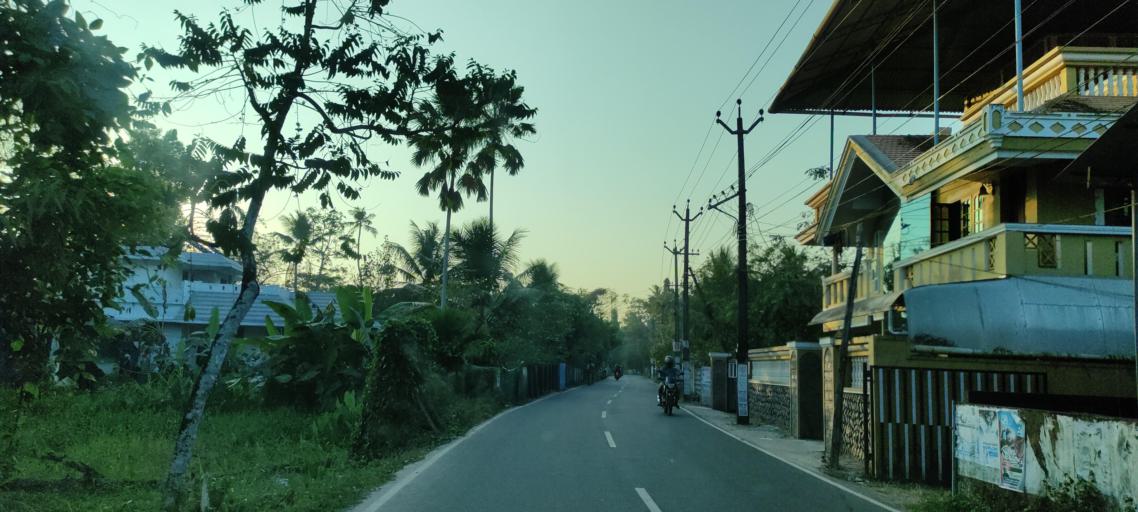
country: IN
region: Kerala
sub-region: Alappuzha
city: Alleppey
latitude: 9.5399
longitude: 76.3417
